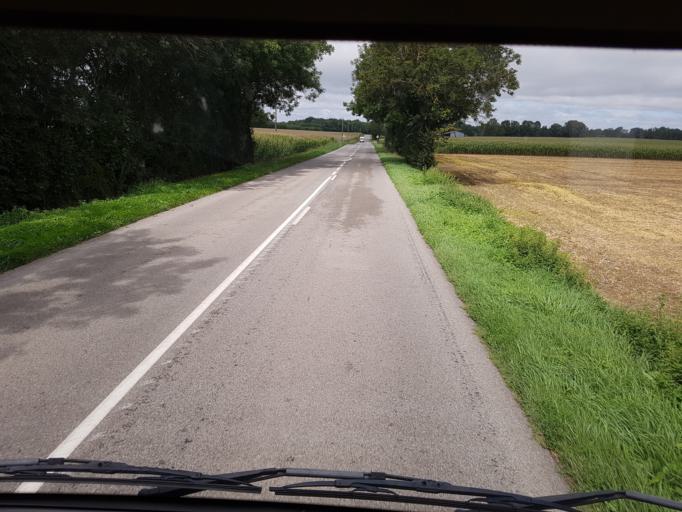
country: FR
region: Rhone-Alpes
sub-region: Departement de l'Ain
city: Perouges
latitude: 45.9129
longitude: 5.1480
